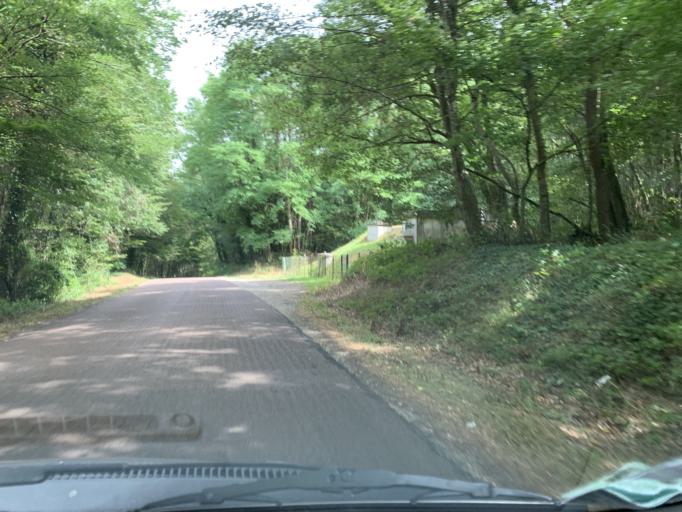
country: FR
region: Bourgogne
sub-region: Departement de la Nievre
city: Clamecy
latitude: 47.4486
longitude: 3.5325
